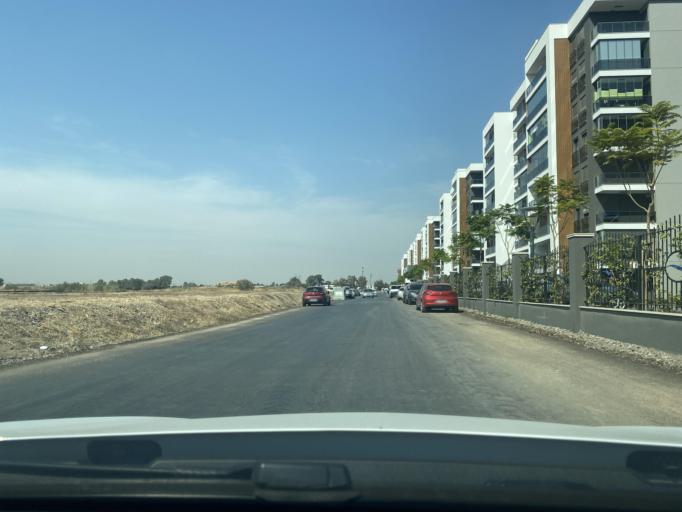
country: TR
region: Izmir
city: Karsiyaka
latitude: 38.4890
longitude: 27.0500
